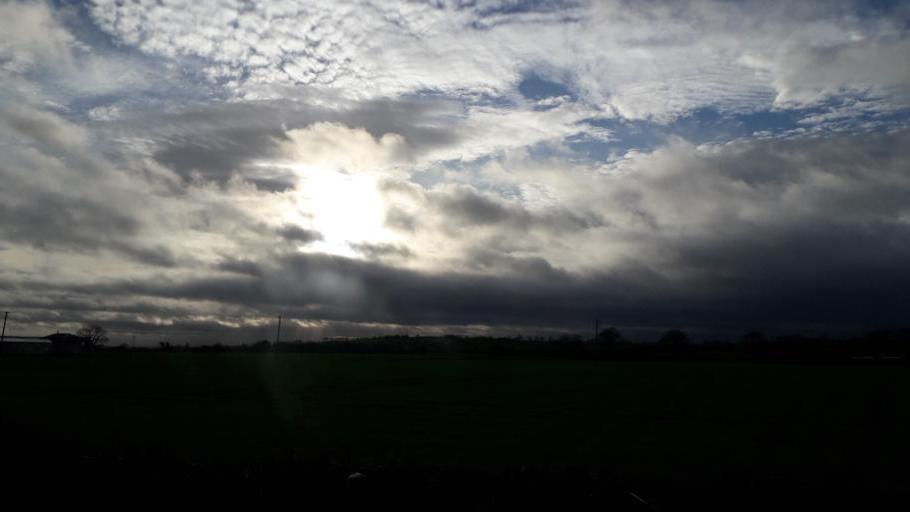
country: IE
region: Leinster
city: Balrothery
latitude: 53.5774
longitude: -6.1576
